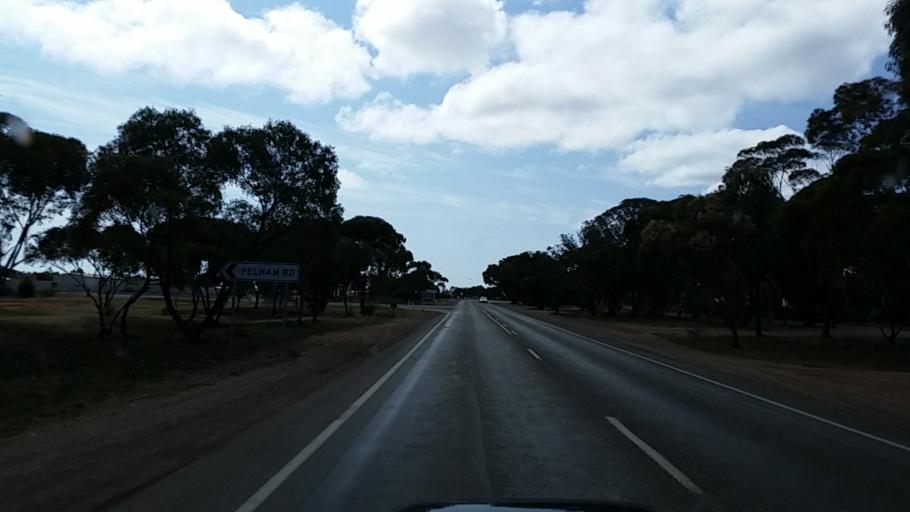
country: AU
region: South Australia
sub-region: Port Pirie City and Dists
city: Port Pirie
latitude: -33.2159
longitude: 138.0109
